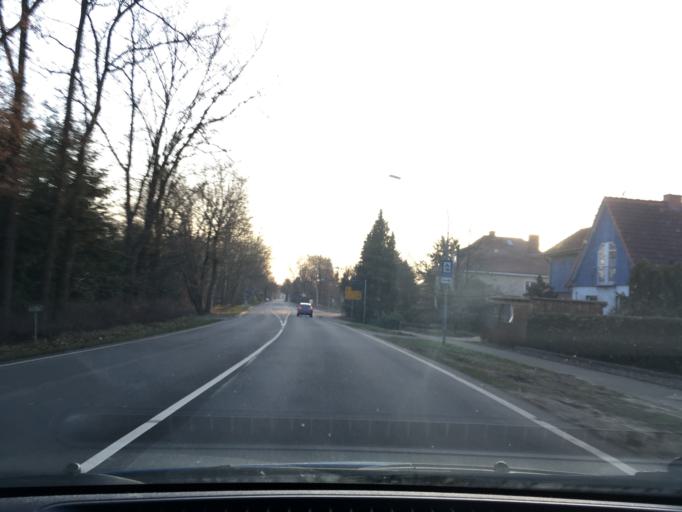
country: DE
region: Lower Saxony
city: Eschede
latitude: 52.7403
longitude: 10.2426
